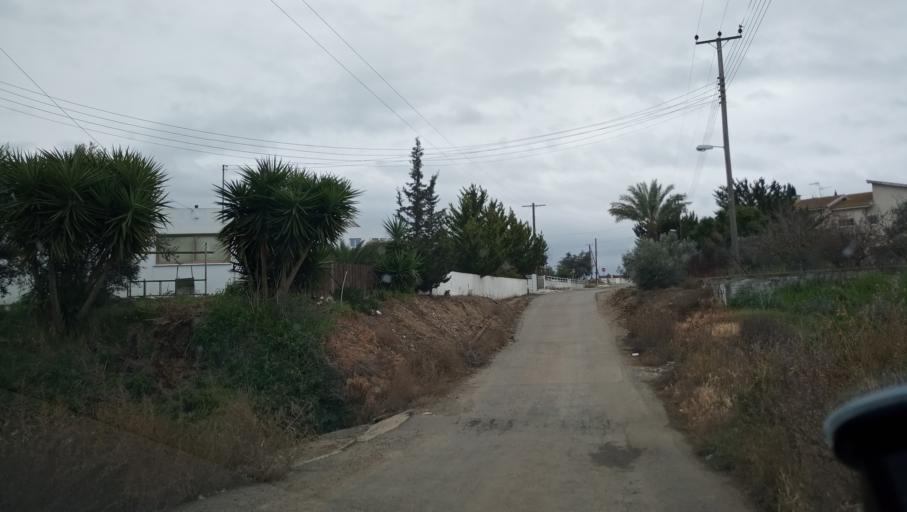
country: CY
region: Lefkosia
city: Kato Deftera
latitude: 35.0812
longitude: 33.2769
